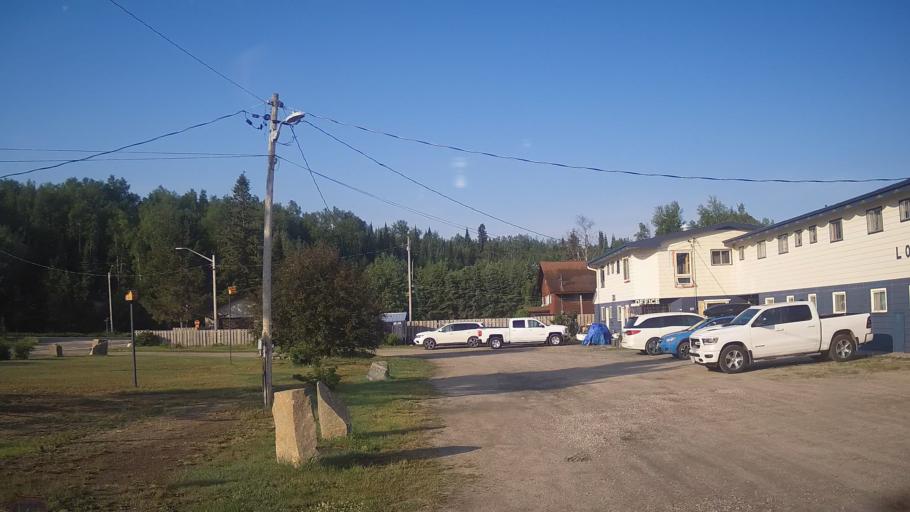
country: CA
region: Ontario
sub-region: Rainy River District
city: Atikokan
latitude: 49.3986
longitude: -91.6677
